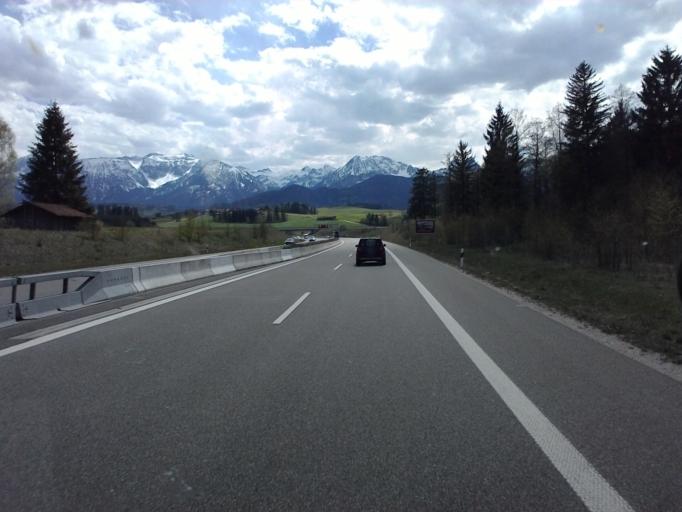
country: DE
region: Bavaria
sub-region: Swabia
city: Hopferau
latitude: 47.6126
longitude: 10.6587
